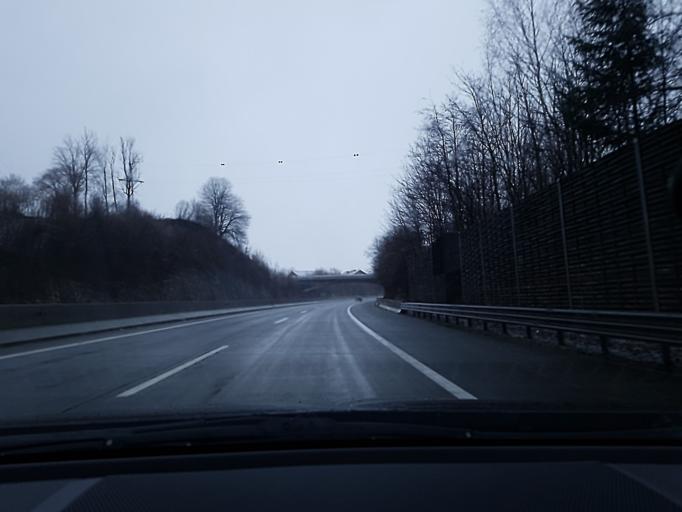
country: AT
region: Salzburg
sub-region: Politischer Bezirk Hallein
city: Kuchl
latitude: 47.6292
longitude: 13.1319
